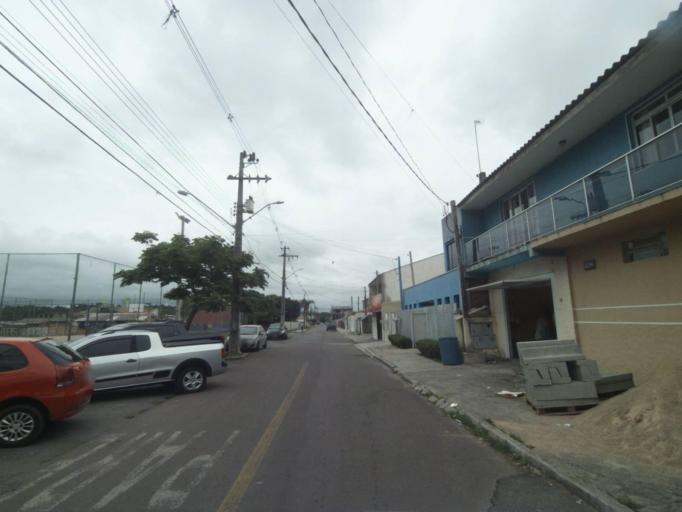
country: BR
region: Parana
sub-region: Araucaria
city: Araucaria
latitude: -25.5301
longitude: -49.3371
